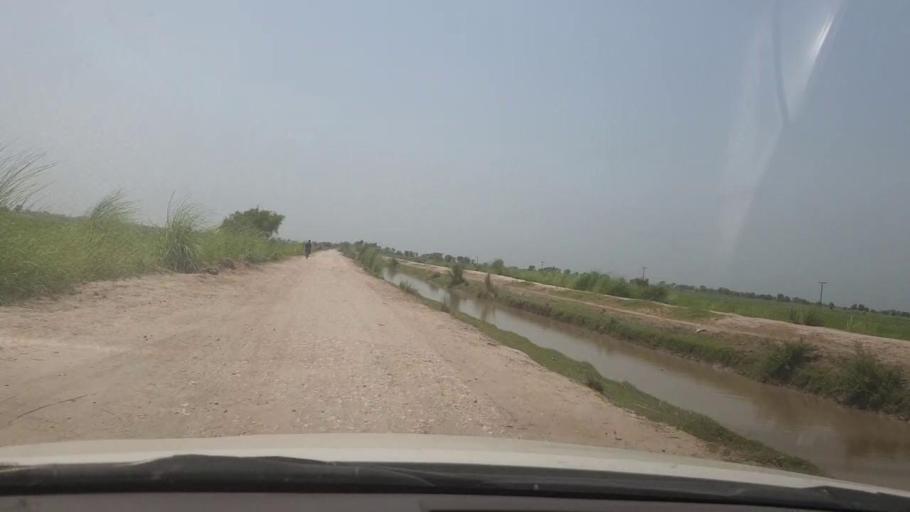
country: PK
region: Sindh
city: Shikarpur
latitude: 28.0516
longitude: 68.5995
